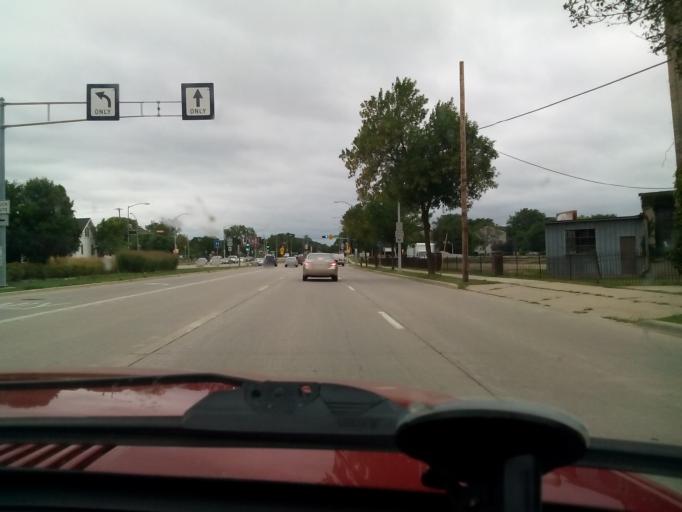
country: US
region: Wisconsin
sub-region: Dane County
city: Maple Bluff
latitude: 43.0950
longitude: -89.3612
